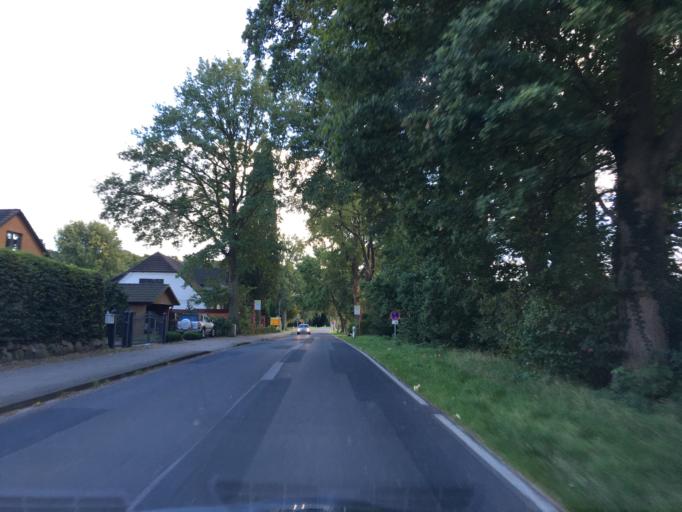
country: DE
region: Lower Saxony
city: Vierhofen
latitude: 53.2600
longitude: 10.2217
